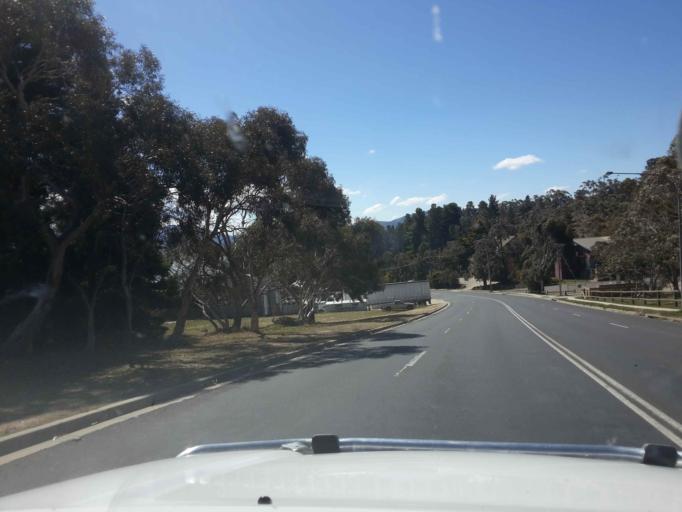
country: AU
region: New South Wales
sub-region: Snowy River
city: Jindabyne
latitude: -36.4177
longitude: 148.6108
